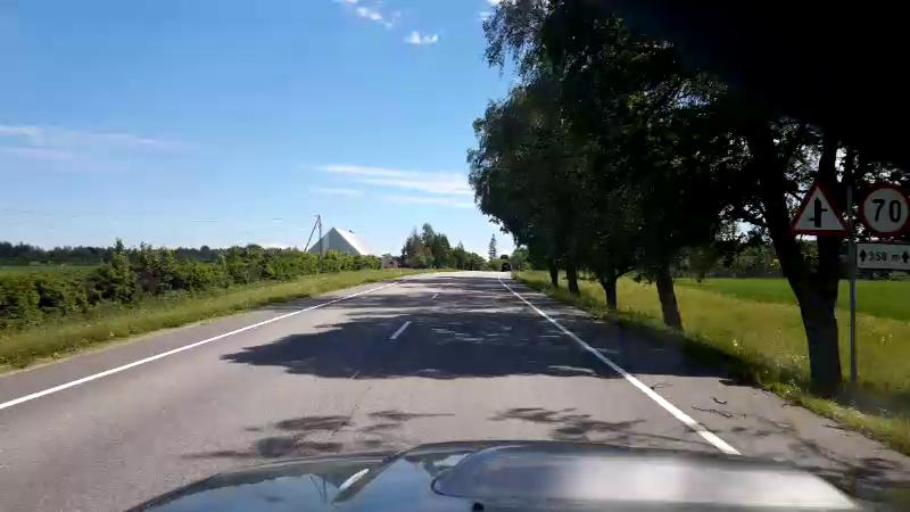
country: EE
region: Jaervamaa
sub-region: Jaerva-Jaani vald
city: Jarva-Jaani
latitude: 59.0057
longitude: 25.9295
